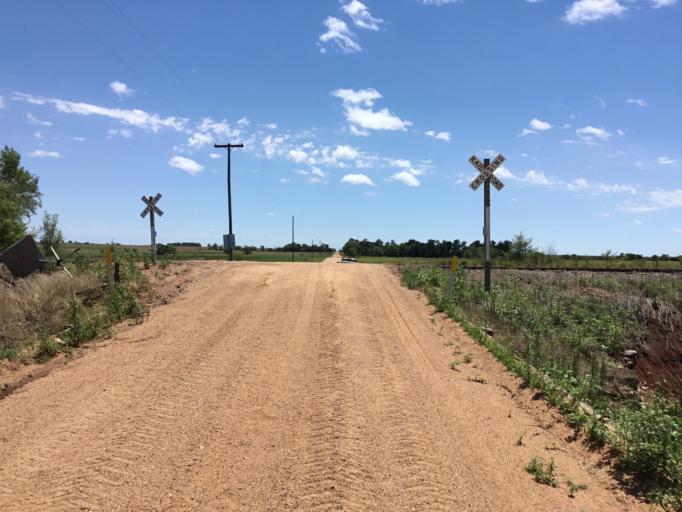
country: US
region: Kansas
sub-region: Sedgwick County
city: Cheney
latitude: 37.6127
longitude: -97.8999
